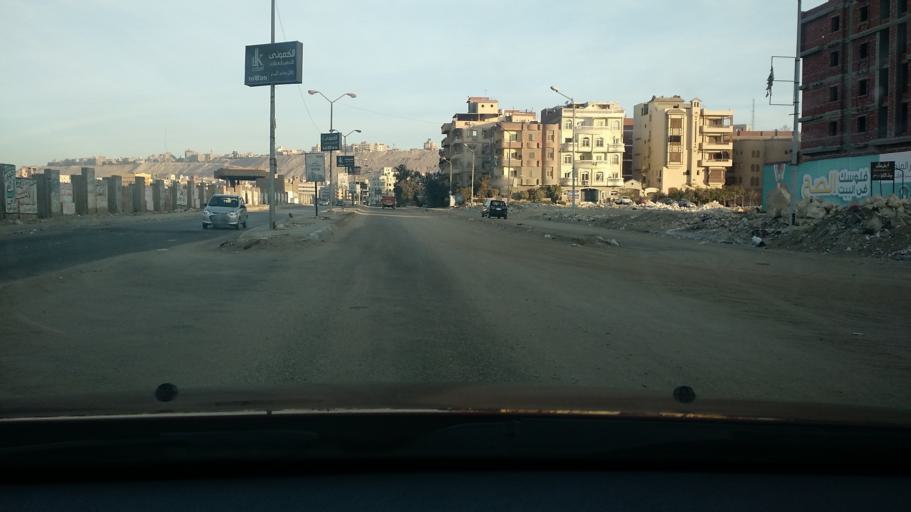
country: EG
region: Muhafazat al Qahirah
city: Cairo
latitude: 29.9986
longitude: 31.2889
